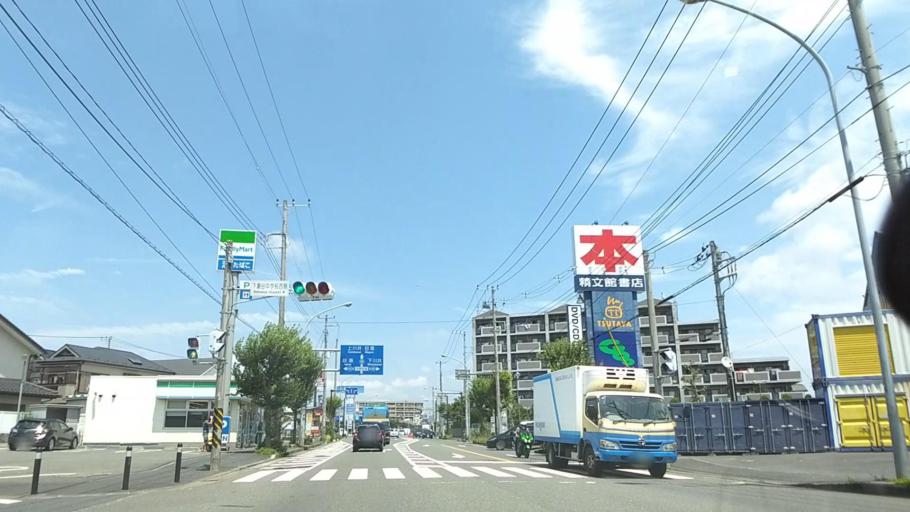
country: JP
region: Kanagawa
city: Minami-rinkan
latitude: 35.4575
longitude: 139.4811
